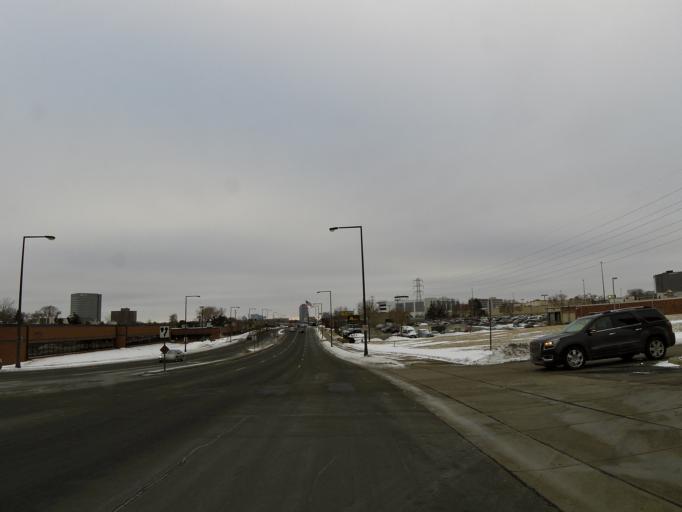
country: US
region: Minnesota
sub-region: Hennepin County
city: Bloomington
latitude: 44.8595
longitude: -93.2902
